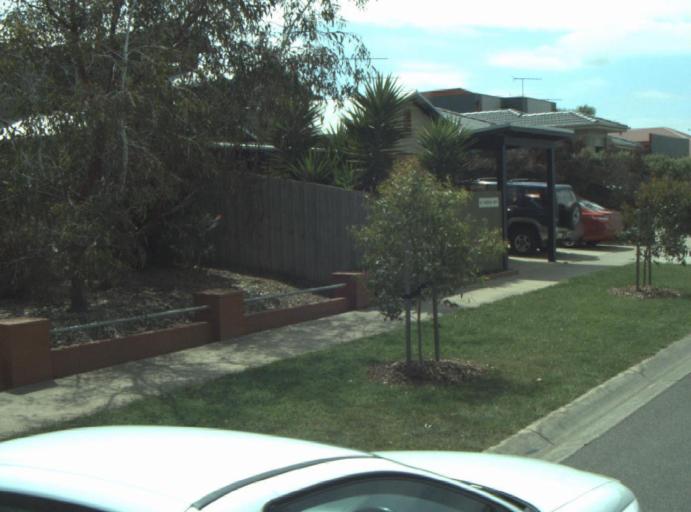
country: AU
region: Victoria
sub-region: Greater Geelong
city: Clifton Springs
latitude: -38.2550
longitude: 144.5518
